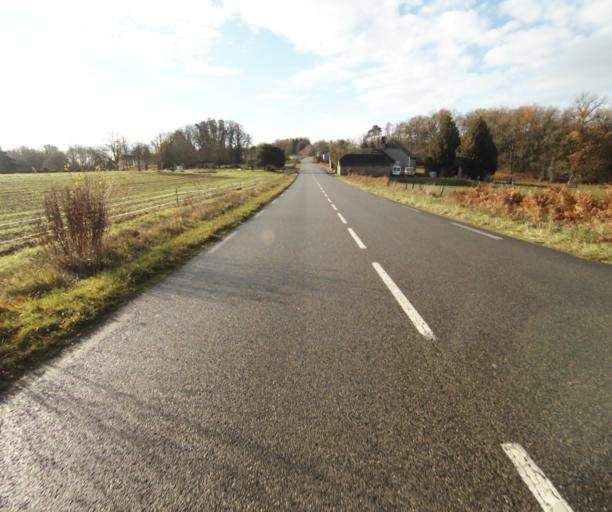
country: FR
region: Limousin
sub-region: Departement de la Correze
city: Saint-Mexant
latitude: 45.2550
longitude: 1.6334
